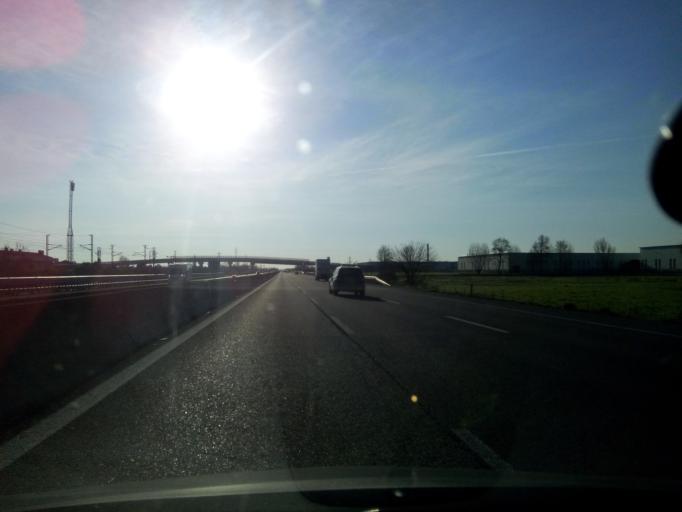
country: IT
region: Emilia-Romagna
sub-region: Provincia di Parma
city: Baganzola
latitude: 44.8544
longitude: 10.2786
